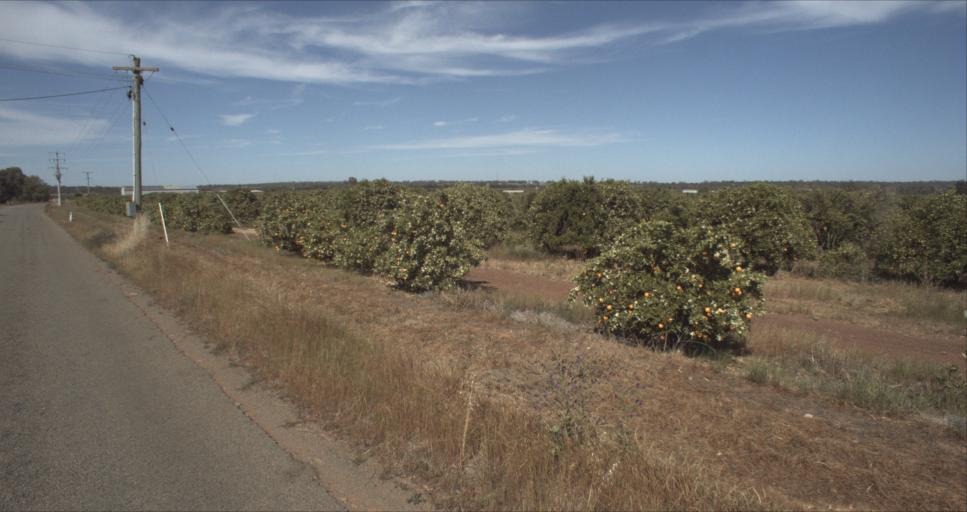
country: AU
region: New South Wales
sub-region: Leeton
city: Leeton
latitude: -34.5807
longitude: 146.4772
